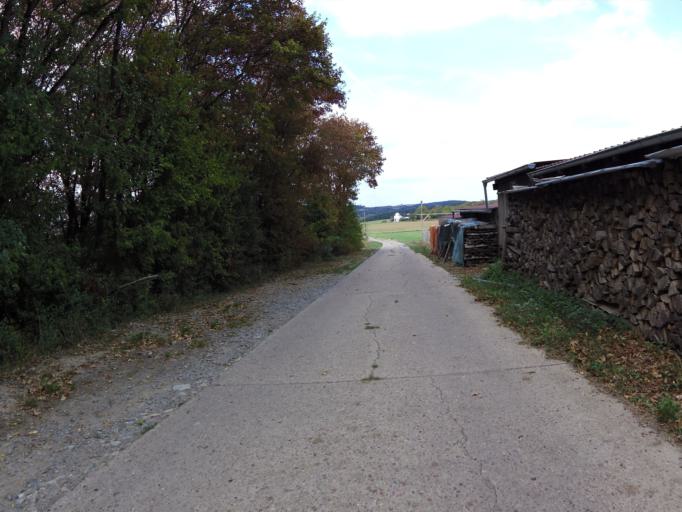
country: DE
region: Bavaria
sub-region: Regierungsbezirk Unterfranken
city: Hettstadt
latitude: 49.7904
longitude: 9.7956
